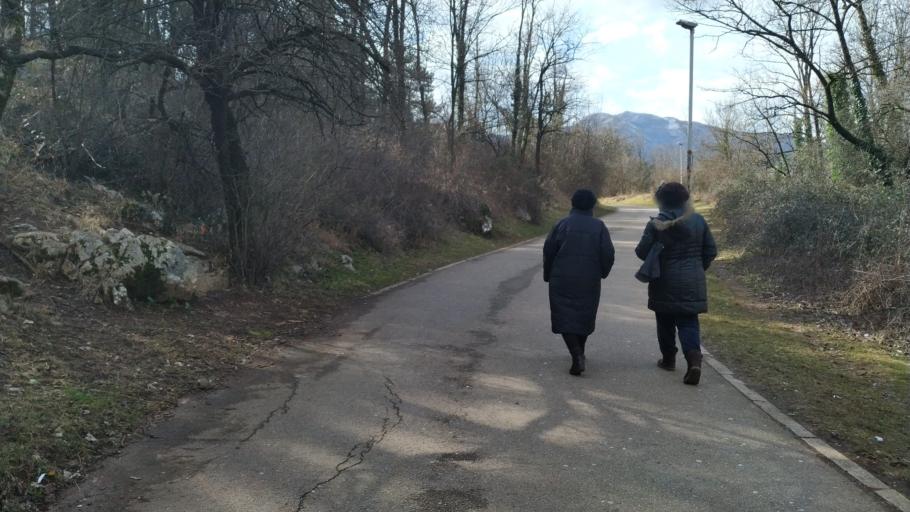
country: ME
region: Opstina Niksic
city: Niksic
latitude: 42.7668
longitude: 18.9565
